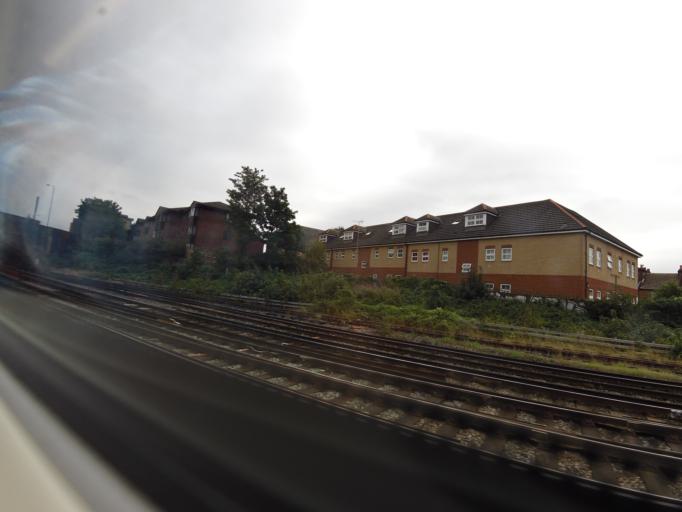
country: GB
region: England
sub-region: Greater London
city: Thornton Heath
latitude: 51.4001
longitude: -0.0731
